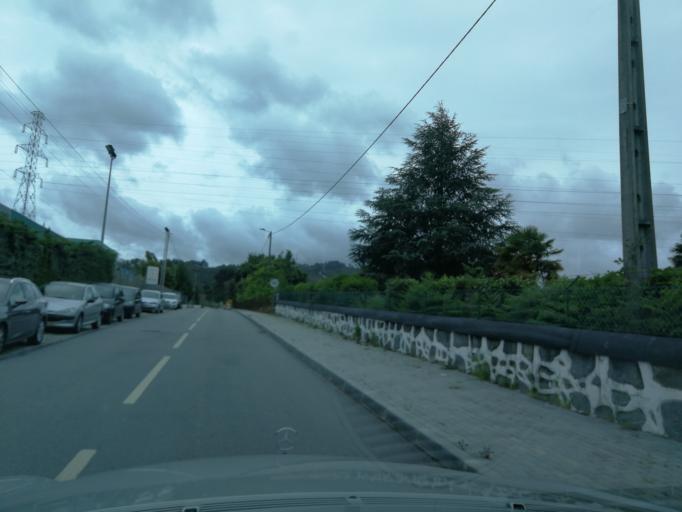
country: PT
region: Braga
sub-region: Braga
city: Adaufe
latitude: 41.6023
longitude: -8.3811
